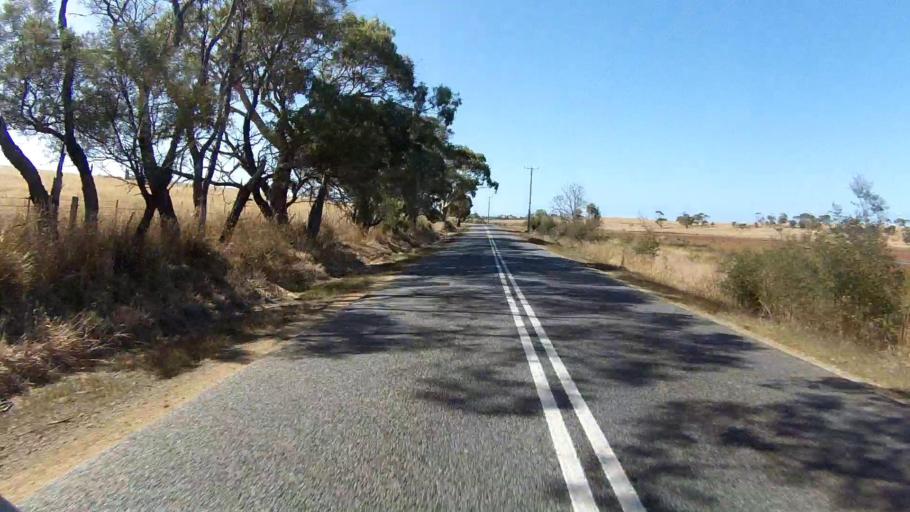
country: AU
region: Tasmania
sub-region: Sorell
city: Sorell
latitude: -42.2786
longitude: 148.0025
